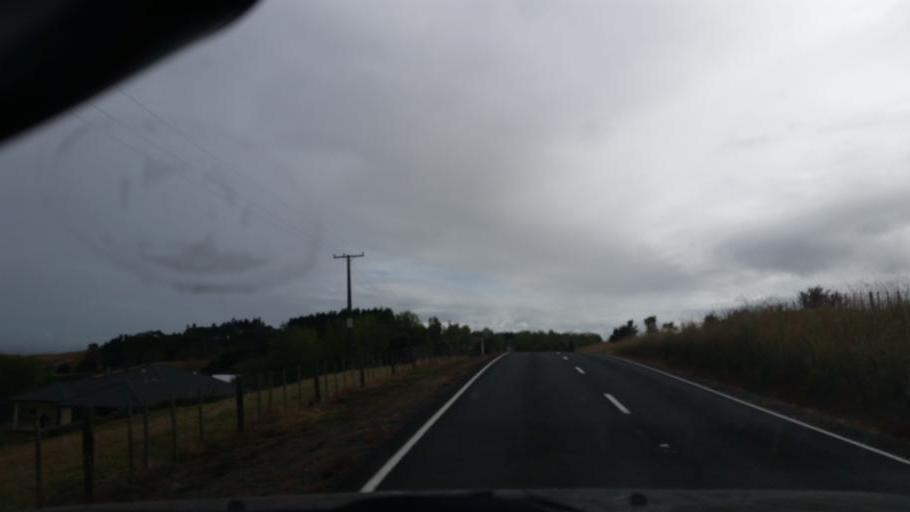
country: NZ
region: Auckland
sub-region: Auckland
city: Wellsford
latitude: -36.2170
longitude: 174.3891
